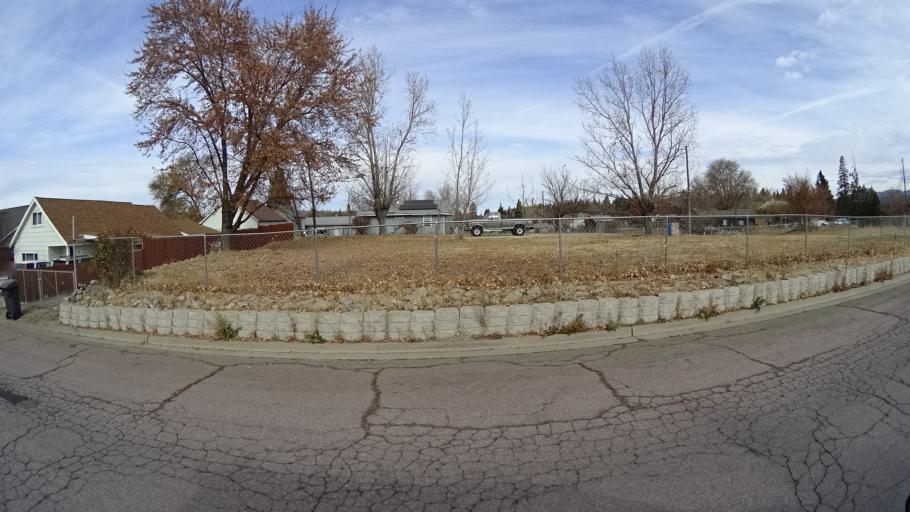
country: US
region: California
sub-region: Siskiyou County
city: Weed
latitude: 41.4360
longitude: -122.3793
